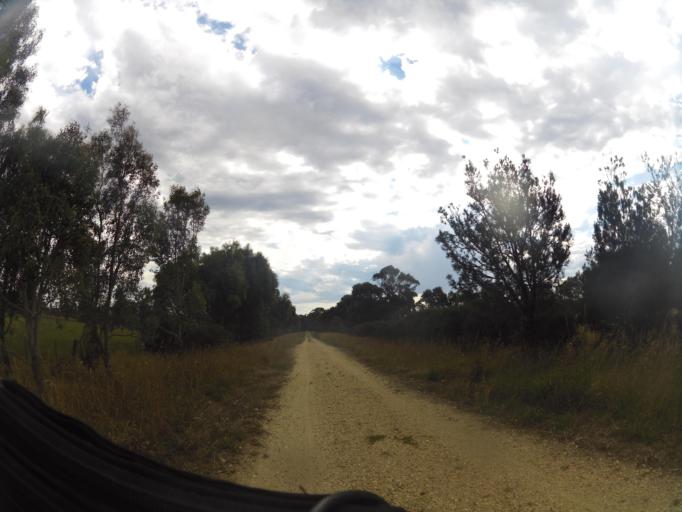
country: AU
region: Victoria
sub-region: Wellington
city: Heyfield
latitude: -38.0487
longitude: 146.6336
